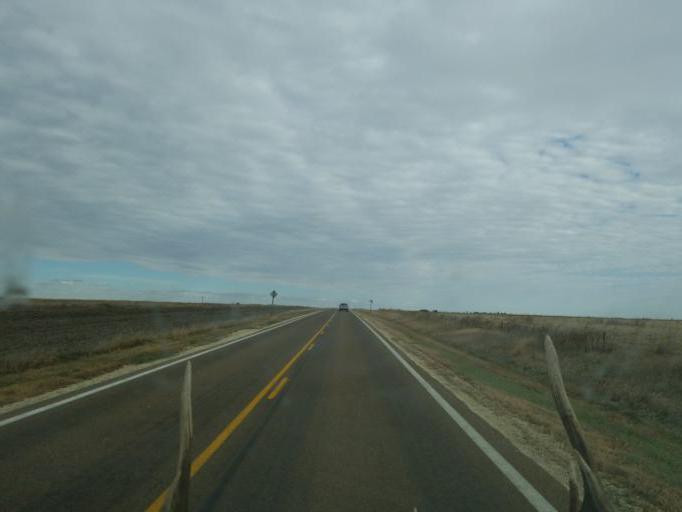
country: US
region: Kansas
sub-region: Logan County
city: Oakley
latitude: 39.0894
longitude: -101.1431
